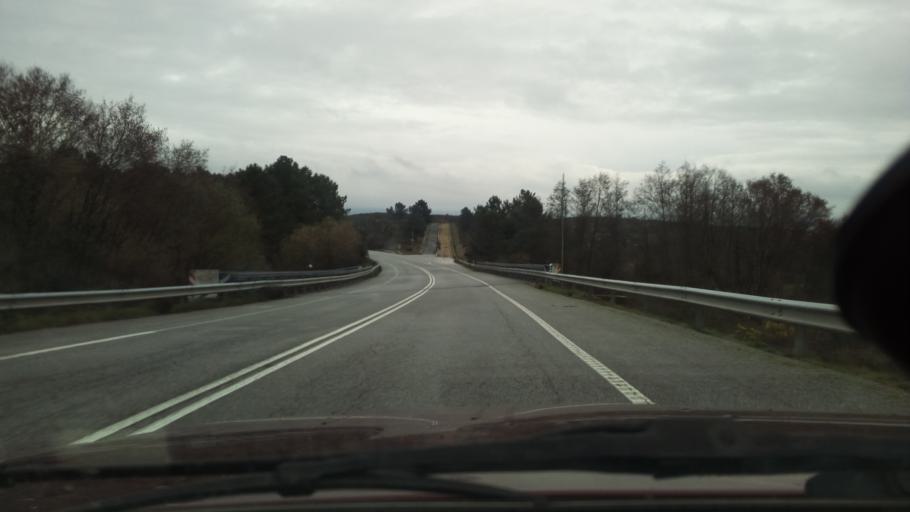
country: PT
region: Guarda
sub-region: Fornos de Algodres
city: Fornos de Algodres
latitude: 40.6071
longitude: -7.5891
